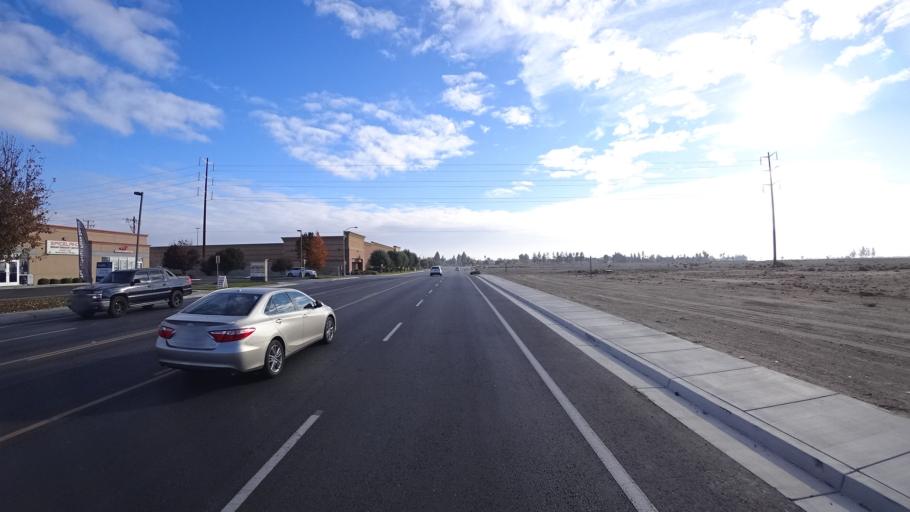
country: US
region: California
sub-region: Kern County
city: Greenacres
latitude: 35.3034
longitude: -119.0971
